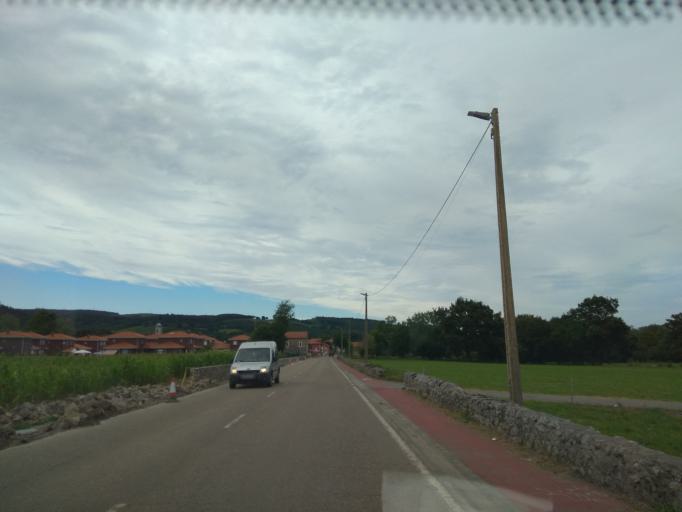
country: ES
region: Cantabria
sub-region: Provincia de Cantabria
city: Hazas de Cesto
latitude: 43.3913
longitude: -3.5887
